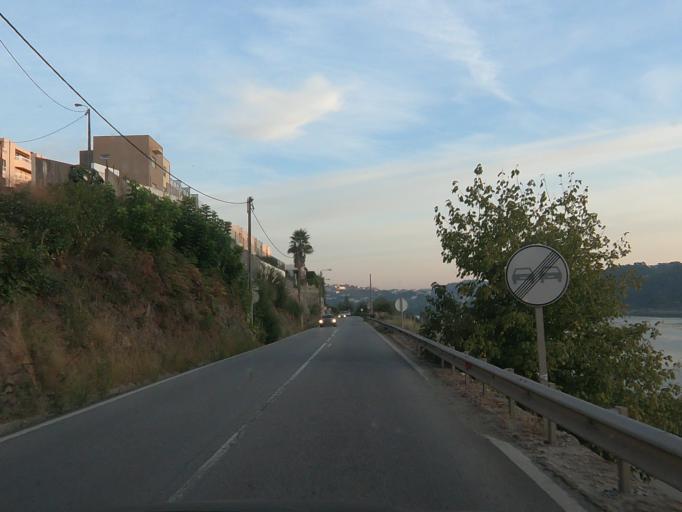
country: PT
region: Porto
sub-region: Gondomar
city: Valbom
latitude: 41.1363
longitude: -8.5709
